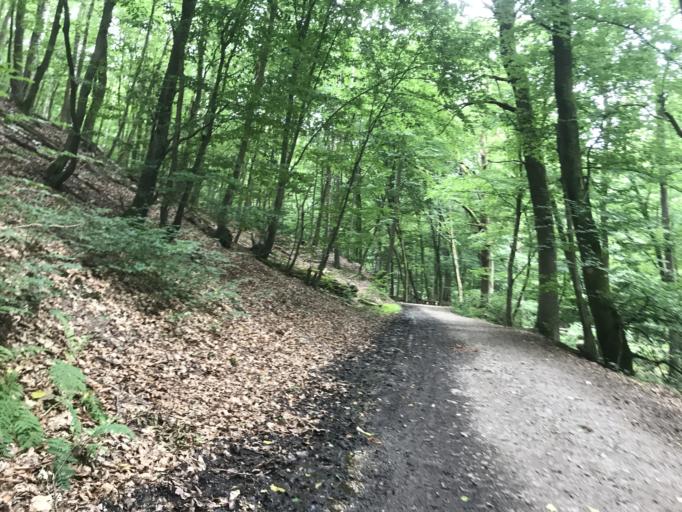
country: DE
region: Rheinland-Pfalz
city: Waldalgesheim
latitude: 49.9850
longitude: 7.8331
